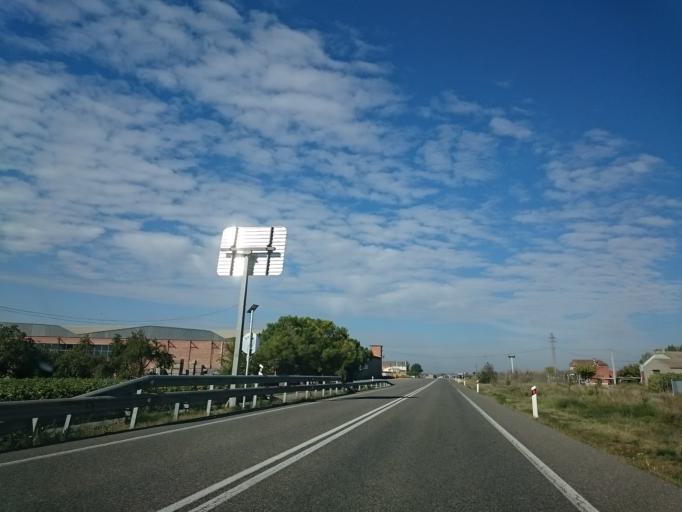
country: ES
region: Catalonia
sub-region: Provincia de Lleida
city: Juneda
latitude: 41.5532
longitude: 0.8144
